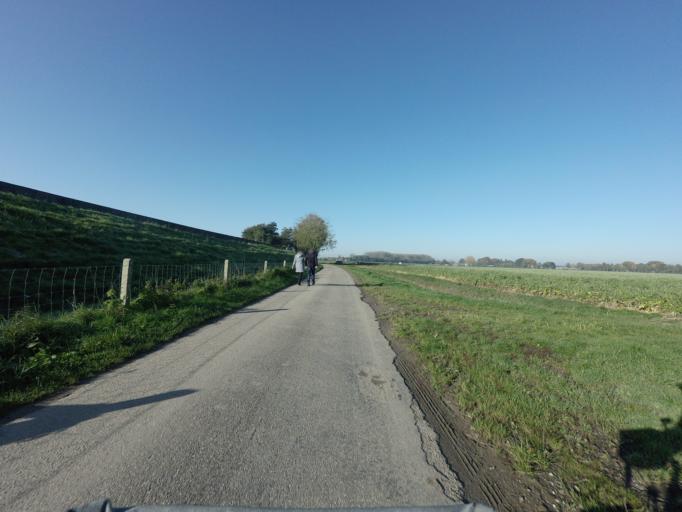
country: NL
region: North Brabant
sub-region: Gemeente Werkendam
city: Werkendam
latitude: 51.7962
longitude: 4.9112
